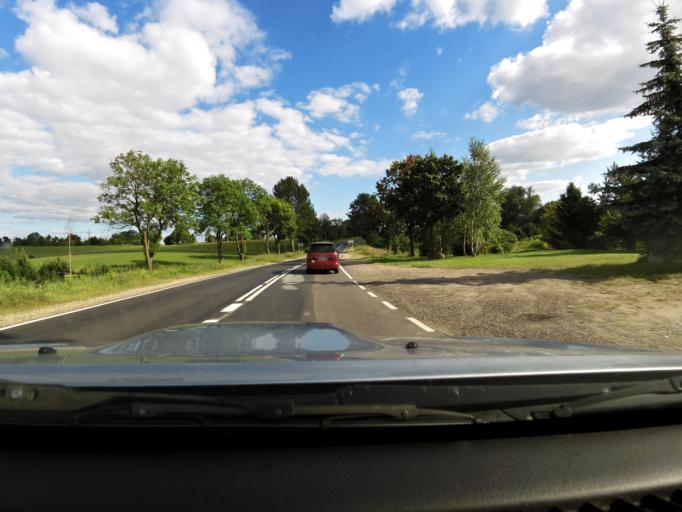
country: PL
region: Podlasie
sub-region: Powiat grajewski
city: Rajgrod
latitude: 53.8708
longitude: 22.6766
